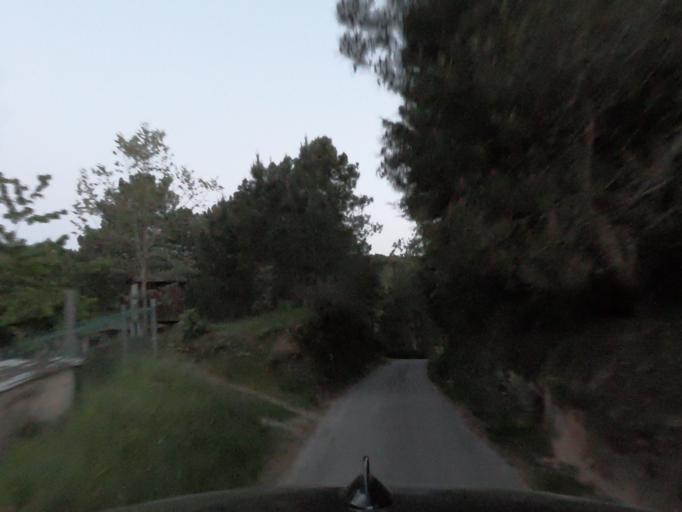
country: PT
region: Vila Real
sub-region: Vila Real
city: Vila Real
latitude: 41.3122
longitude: -7.6822
